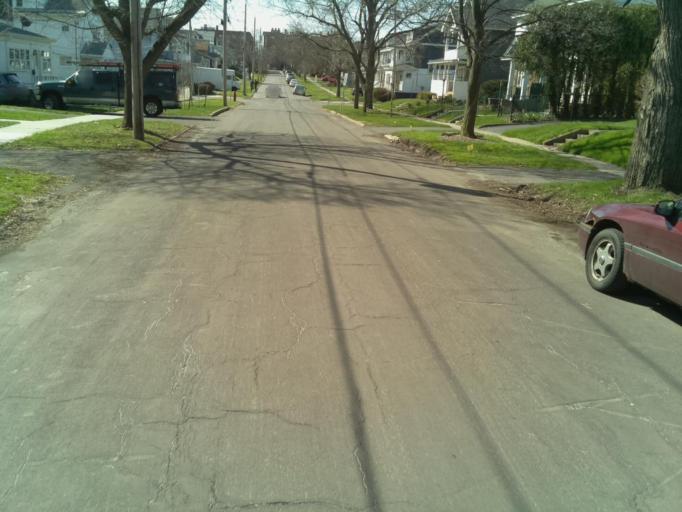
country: US
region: New York
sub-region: Onondaga County
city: Lyncourt
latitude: 43.0722
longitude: -76.1042
